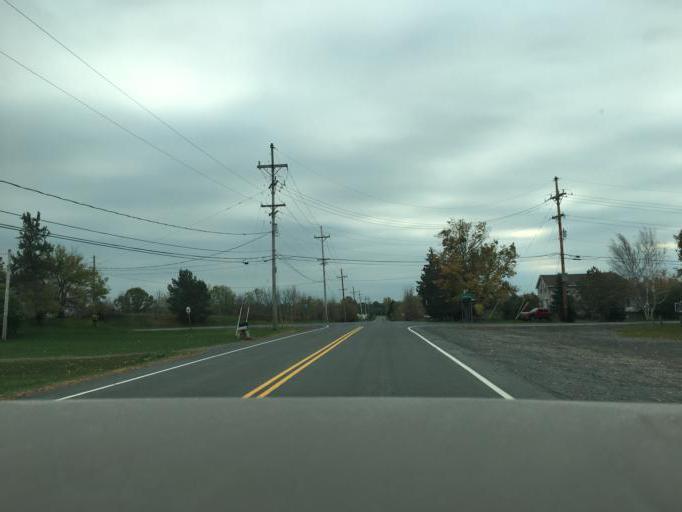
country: US
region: New York
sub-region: Ontario County
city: Victor
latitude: 42.9871
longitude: -77.3261
